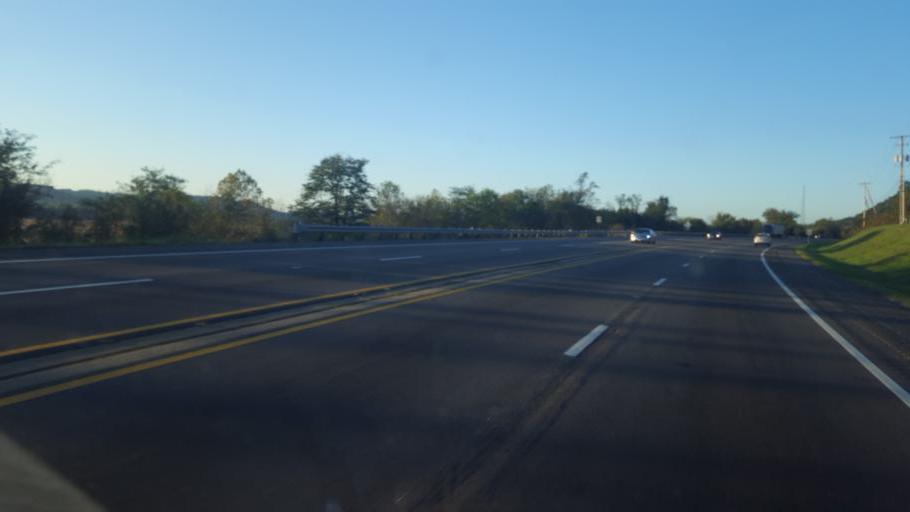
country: US
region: Ohio
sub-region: Scioto County
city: Rosemount
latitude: 38.7945
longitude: -82.9858
